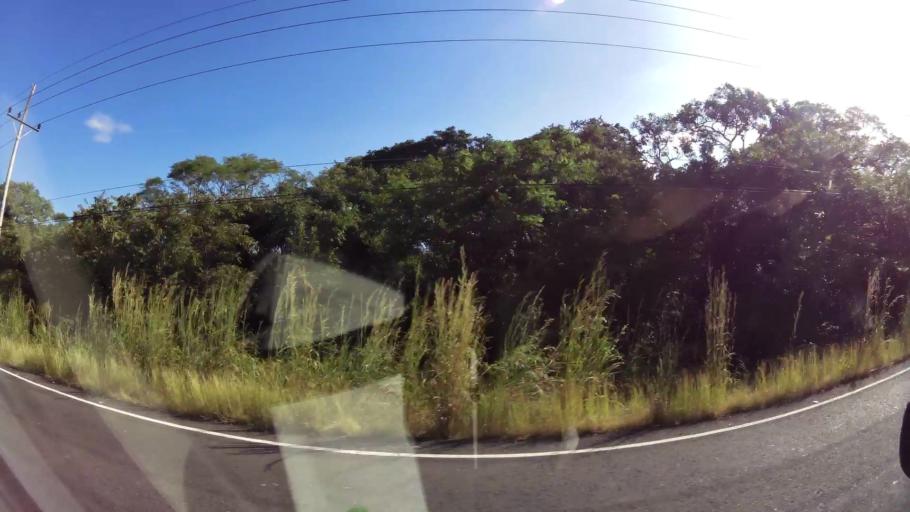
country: CR
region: Guanacaste
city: Sardinal
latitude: 10.5665
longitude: -85.6006
